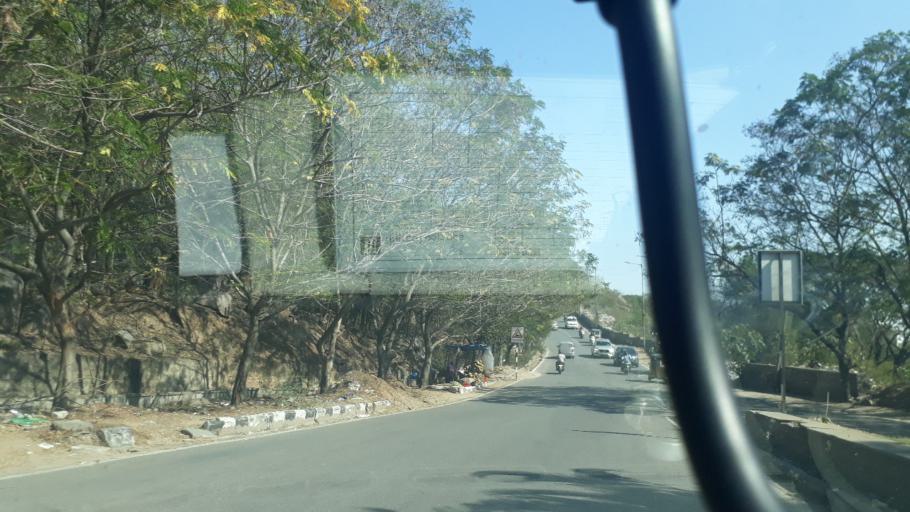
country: IN
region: Telangana
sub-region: Rangareddi
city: Kukatpalli
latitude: 17.4182
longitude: 78.3956
